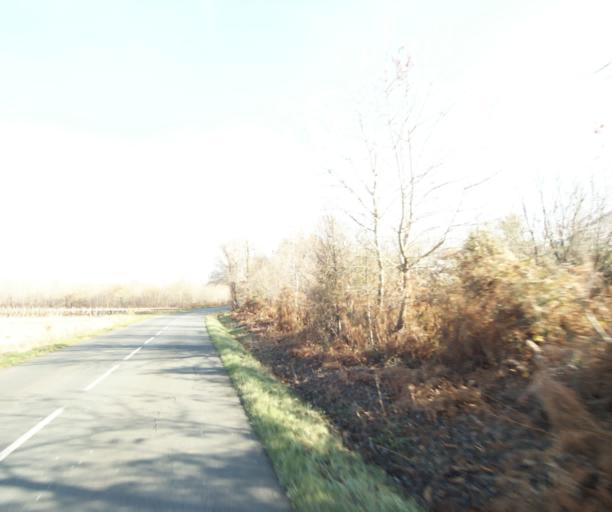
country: FR
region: Poitou-Charentes
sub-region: Departement de la Charente-Maritime
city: Ecoyeux
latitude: 45.7664
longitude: -0.5154
